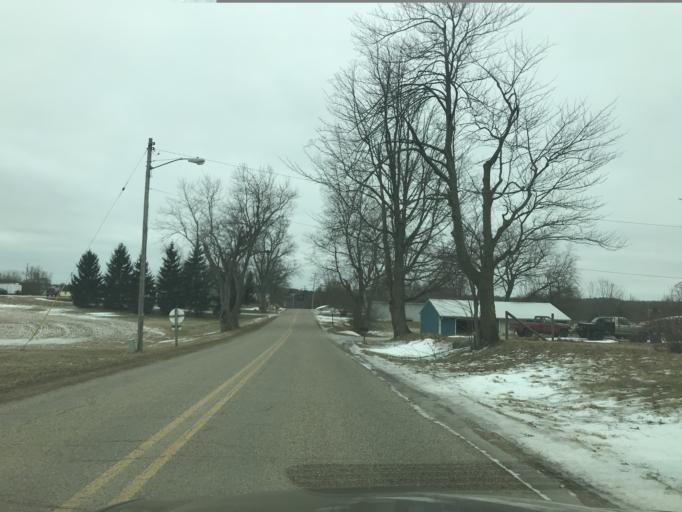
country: US
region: Michigan
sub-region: Jackson County
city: Brooklyn
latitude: 42.0665
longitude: -84.3260
